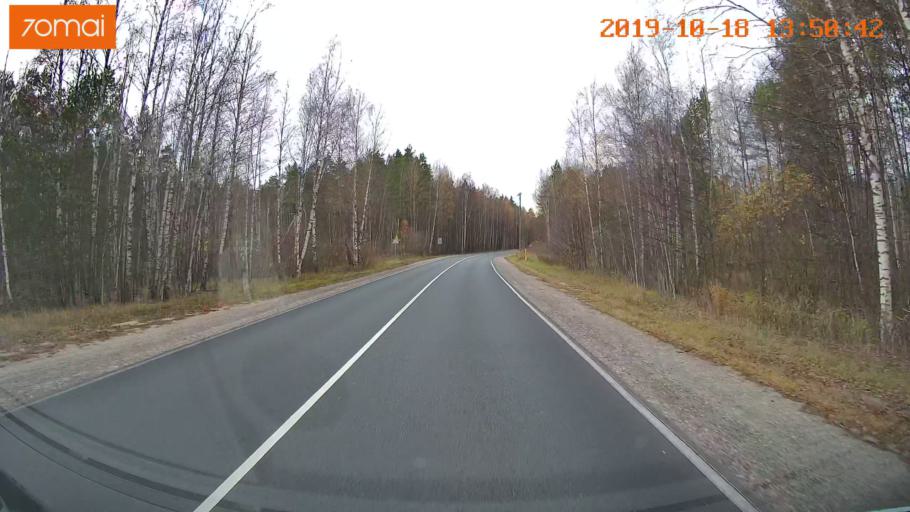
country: RU
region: Moskovskaya
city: Radovitskiy
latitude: 55.0095
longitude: 39.9678
